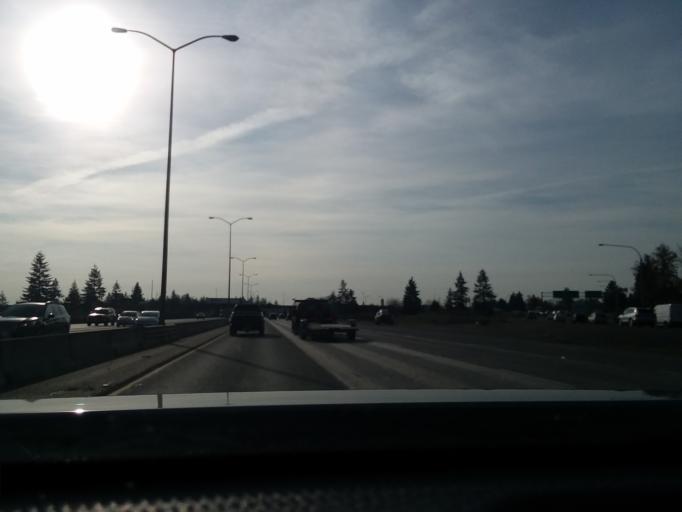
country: US
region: Washington
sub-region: Pierce County
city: McChord Air Force Base
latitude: 47.1656
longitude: -122.4772
